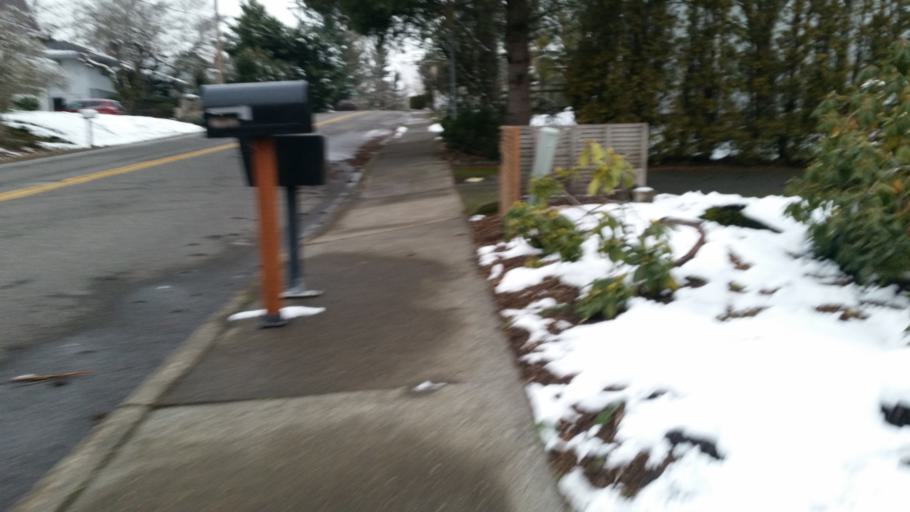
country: US
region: Oregon
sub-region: Washington County
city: Garden Home-Whitford
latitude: 45.4769
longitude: -122.7128
